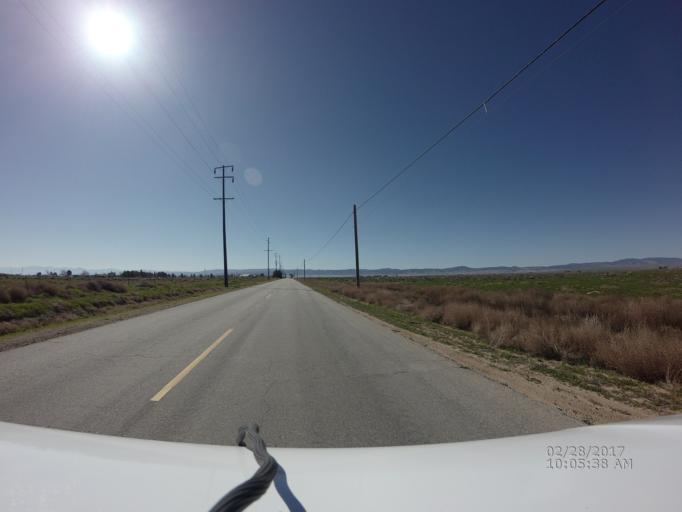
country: US
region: California
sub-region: Kern County
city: Rosamond
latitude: 34.7942
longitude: -118.2903
